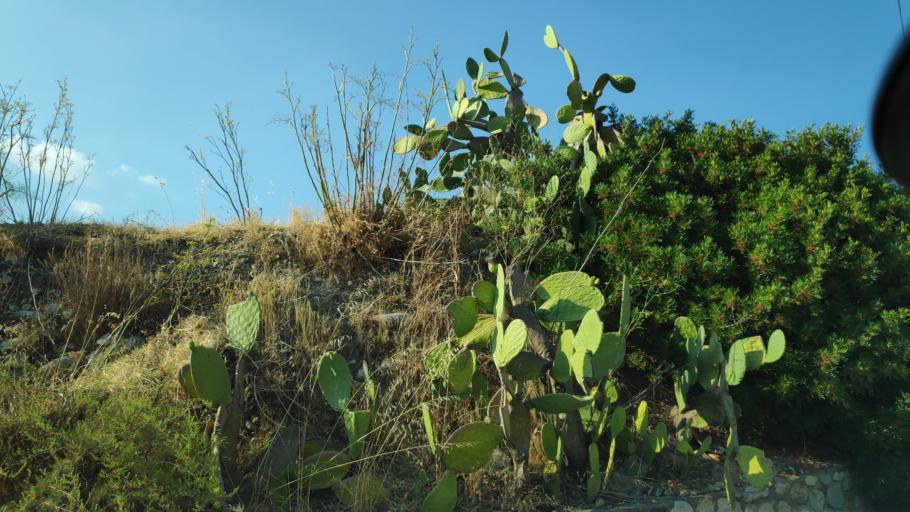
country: IT
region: Calabria
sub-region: Provincia di Catanzaro
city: Guardavalle
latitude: 38.5113
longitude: 16.5033
